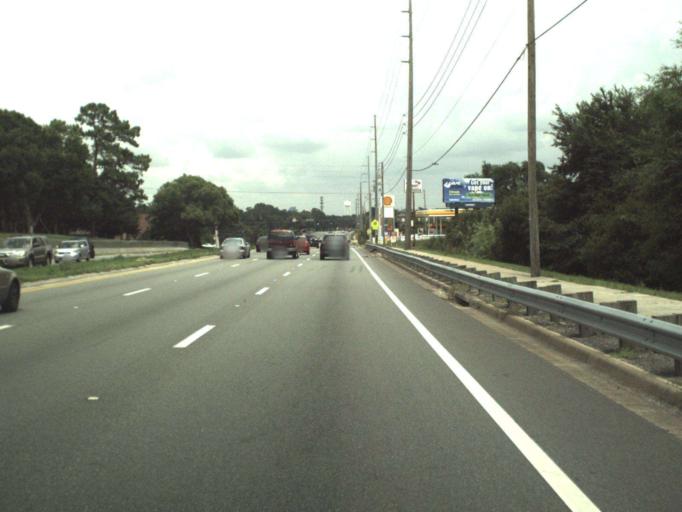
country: US
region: Florida
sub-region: Seminole County
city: Forest City
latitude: 28.6694
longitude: -81.4462
